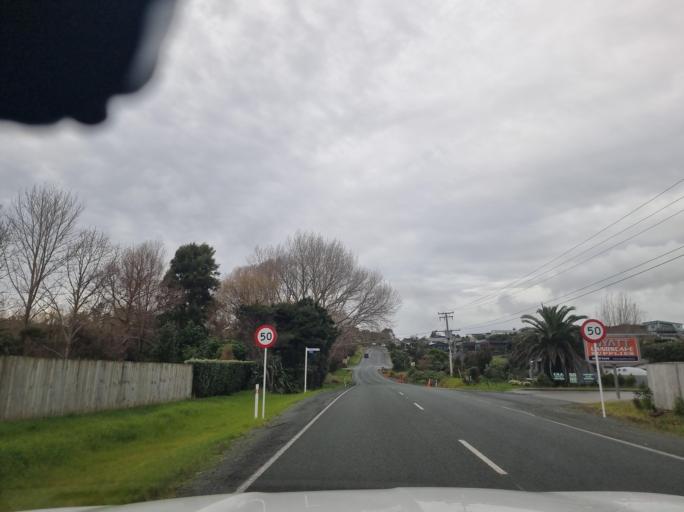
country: NZ
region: Auckland
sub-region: Auckland
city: Wellsford
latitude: -36.0847
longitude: 174.5759
